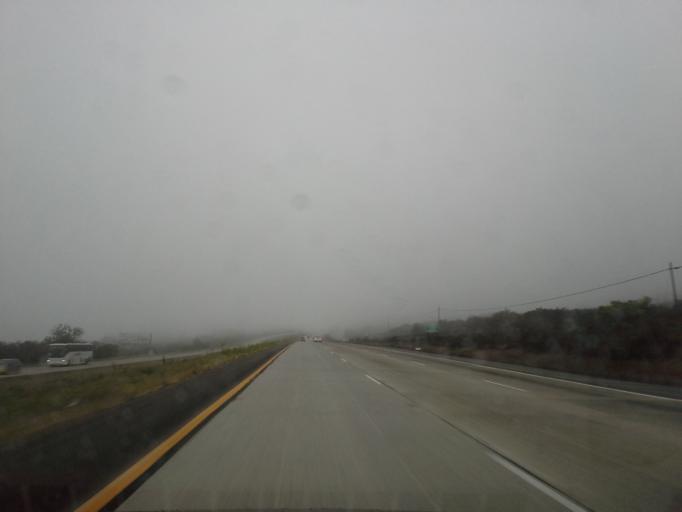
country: US
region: California
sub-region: San Diego County
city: Alpine
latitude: 32.8373
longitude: -116.7096
